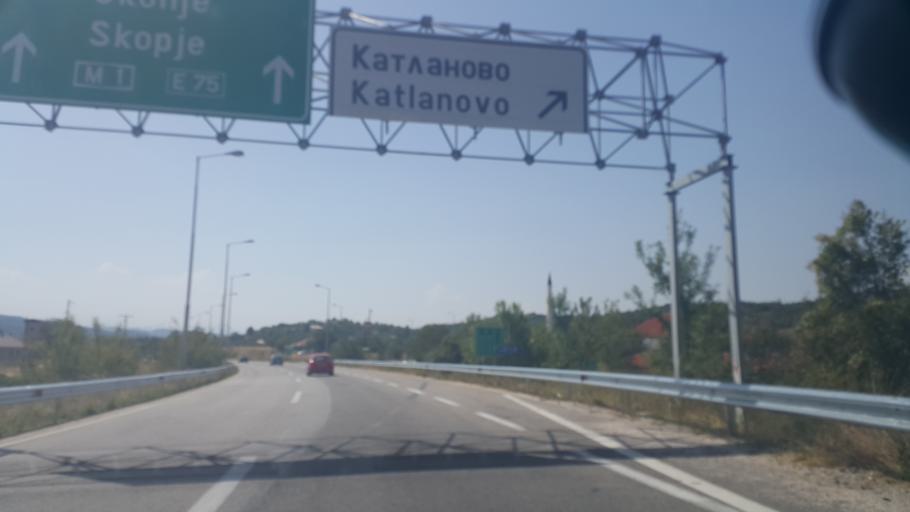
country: MK
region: Petrovec
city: Sredno Konjare
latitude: 41.8948
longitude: 21.6846
